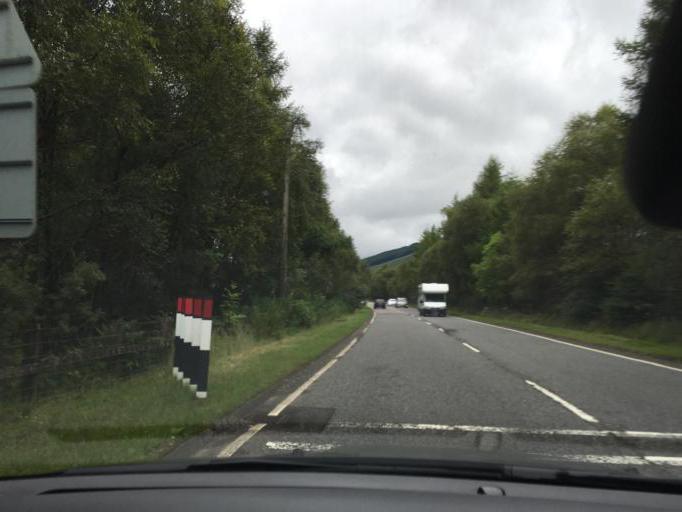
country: GB
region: Scotland
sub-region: Argyll and Bute
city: Garelochhead
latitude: 56.4147
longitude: -4.6627
